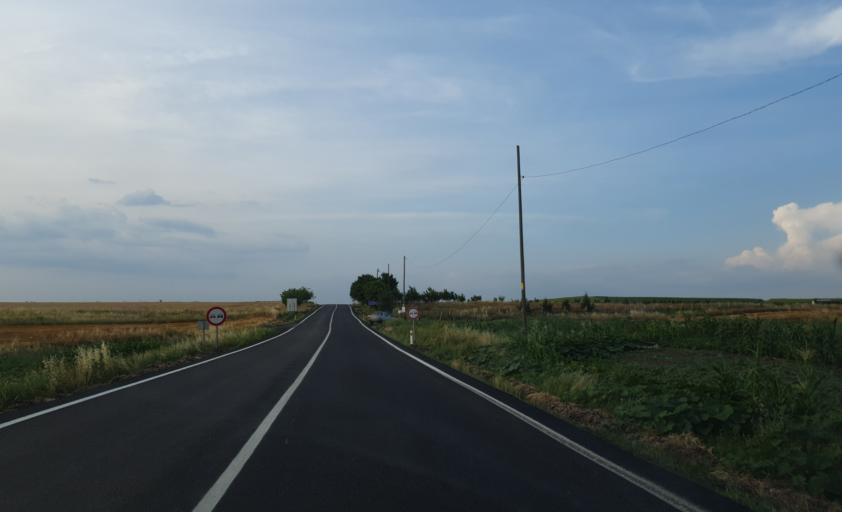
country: TR
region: Tekirdag
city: Hayrabolu
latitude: 41.2945
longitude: 27.1351
